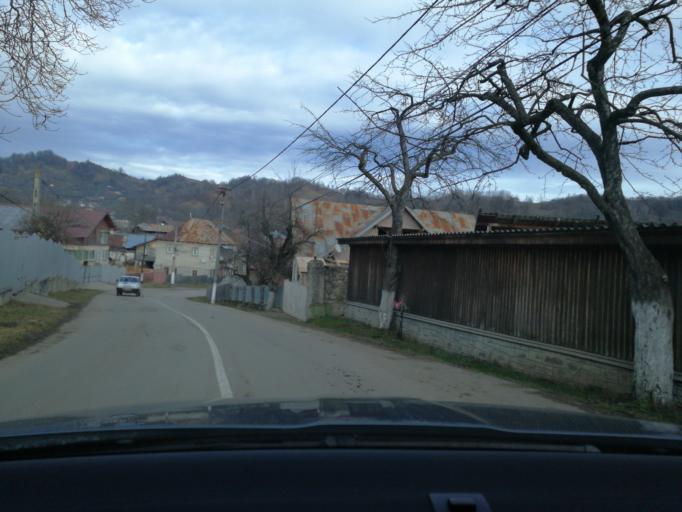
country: RO
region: Prahova
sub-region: Comuna Adunati
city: Ocina de Sus
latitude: 45.1817
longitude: 25.6050
